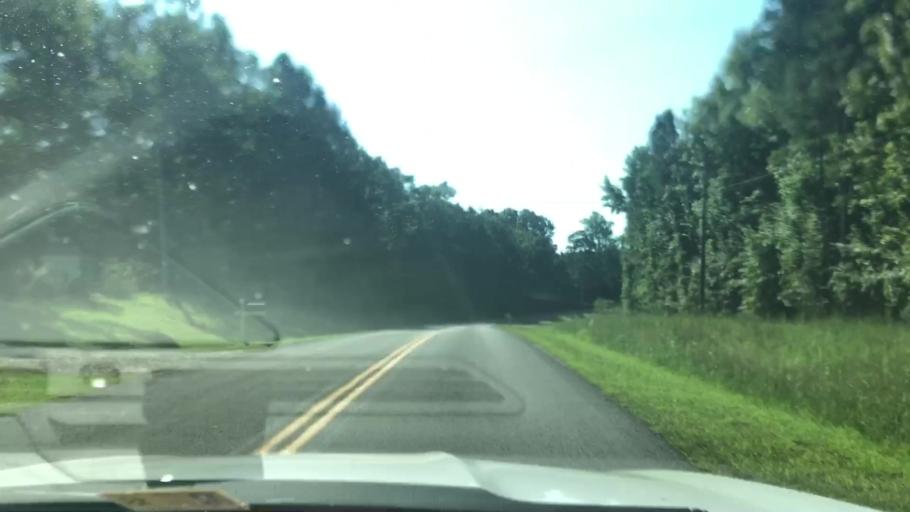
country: US
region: Virginia
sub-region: New Kent County
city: New Kent
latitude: 37.4668
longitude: -76.9301
